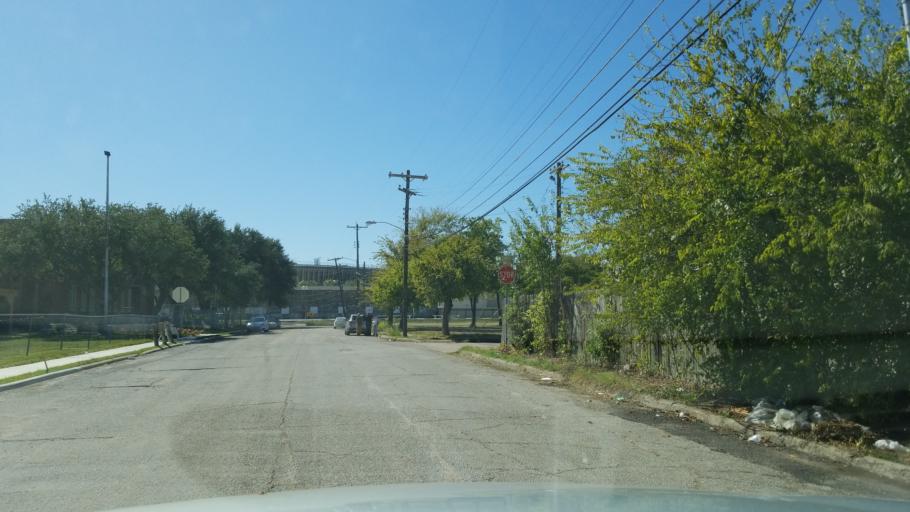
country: US
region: Texas
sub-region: Dallas County
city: Dallas
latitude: 32.7834
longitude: -96.7590
